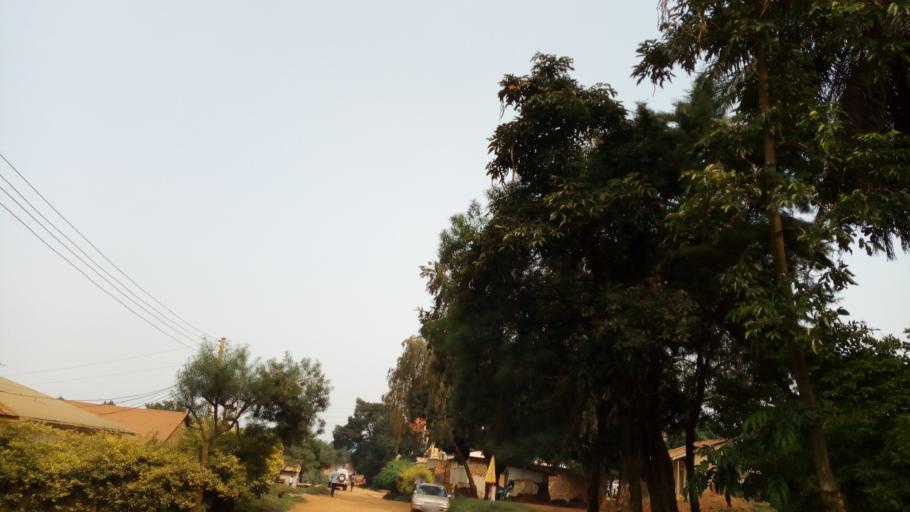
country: UG
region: Central Region
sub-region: Wakiso District
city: Kireka
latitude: 0.3159
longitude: 32.6487
